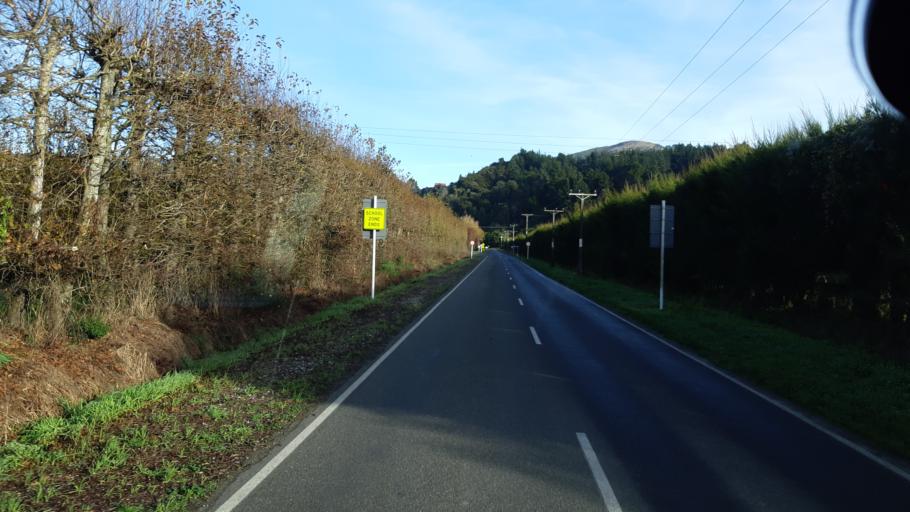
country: NZ
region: Tasman
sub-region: Tasman District
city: Motueka
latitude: -41.0959
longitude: 172.9703
